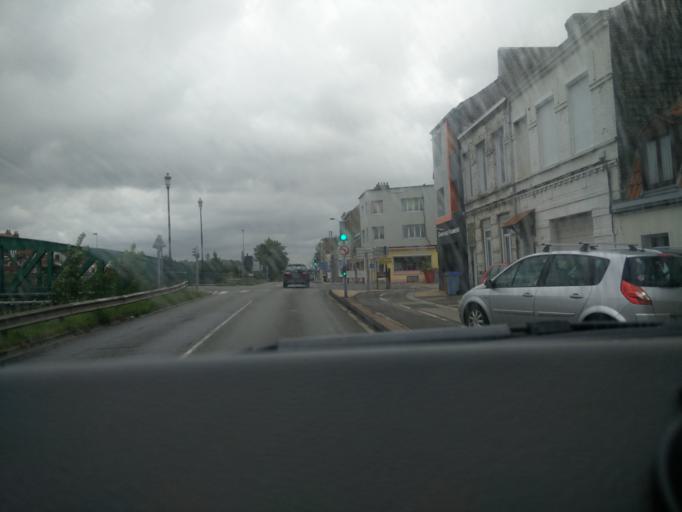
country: FR
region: Nord-Pas-de-Calais
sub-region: Departement du Nord
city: Dunkerque
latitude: 51.0183
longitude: 2.3767
